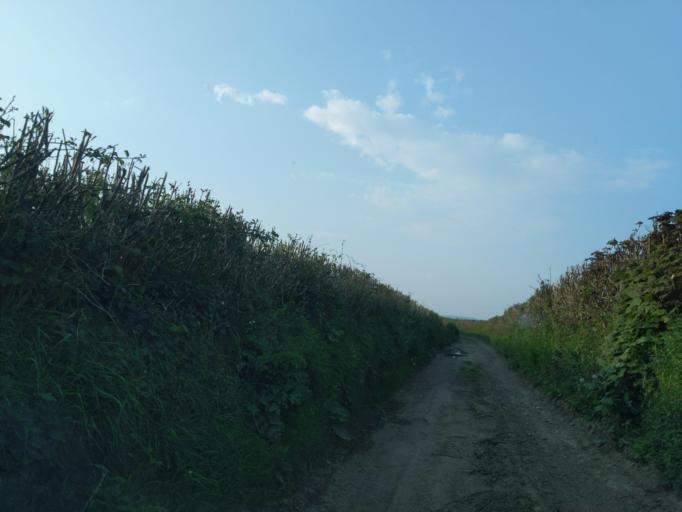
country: GB
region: England
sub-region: Devon
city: Yealmpton
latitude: 50.3547
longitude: -4.0388
